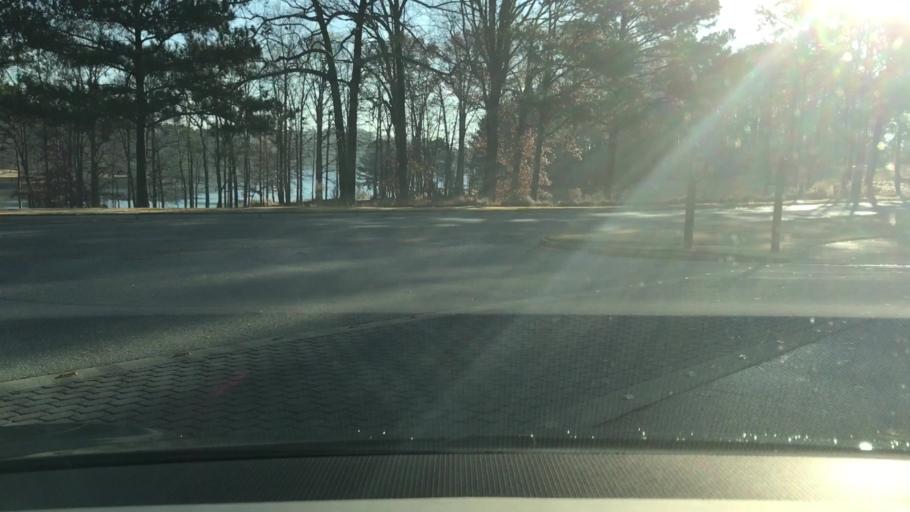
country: US
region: Georgia
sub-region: Gwinnett County
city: Buford
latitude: 34.1737
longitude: -84.0251
